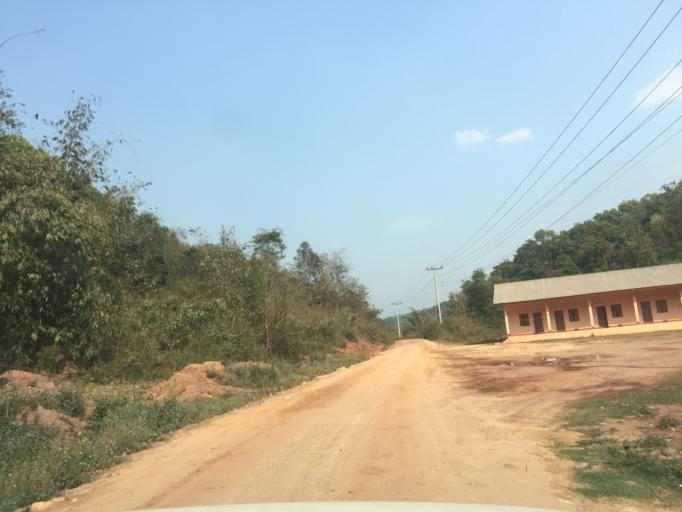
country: LA
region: Oudomxai
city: Muang La
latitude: 21.0741
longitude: 101.8228
